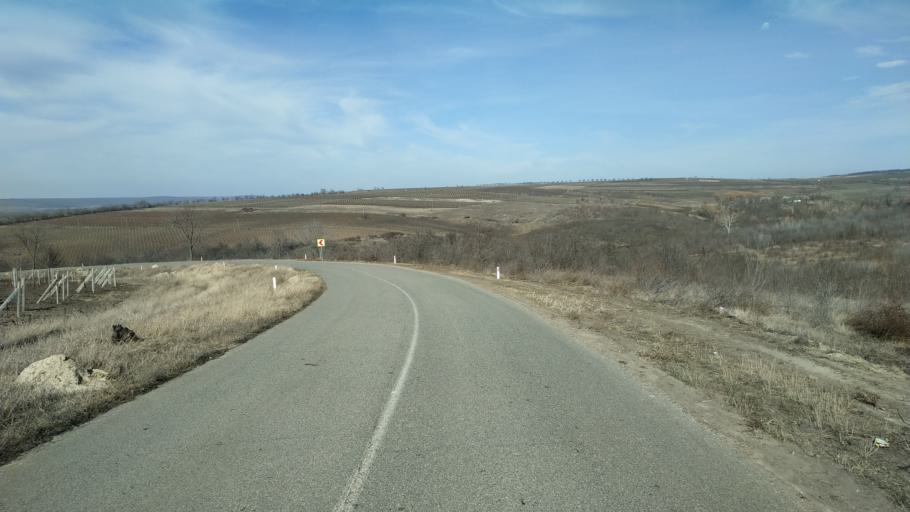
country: MD
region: Nisporeni
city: Nisporeni
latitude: 46.9562
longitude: 28.2356
